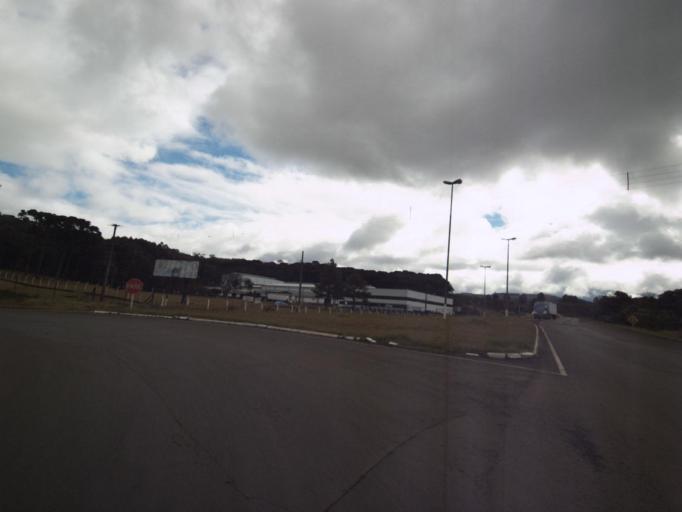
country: BR
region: Santa Catarina
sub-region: Concordia
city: Concordia
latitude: -27.2240
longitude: -51.9494
